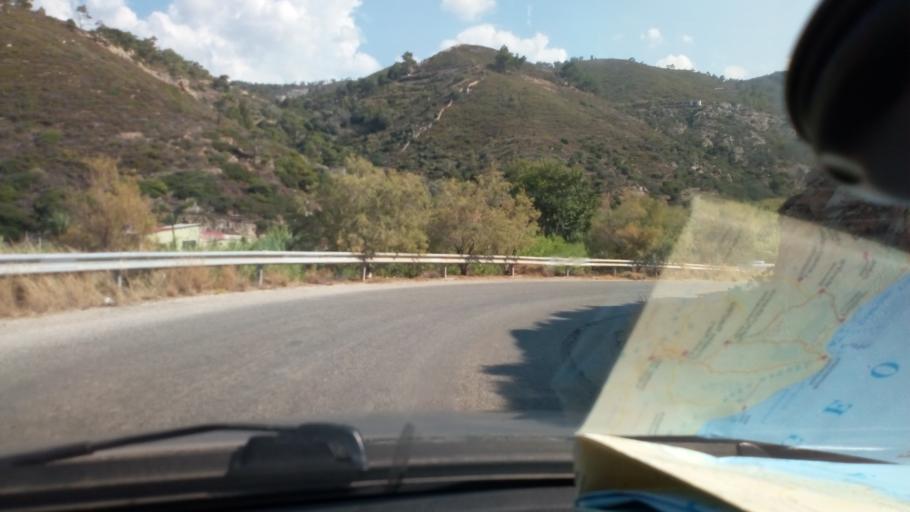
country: GR
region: North Aegean
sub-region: Nomos Samou
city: Agios Kirykos
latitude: 37.6289
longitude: 26.0892
